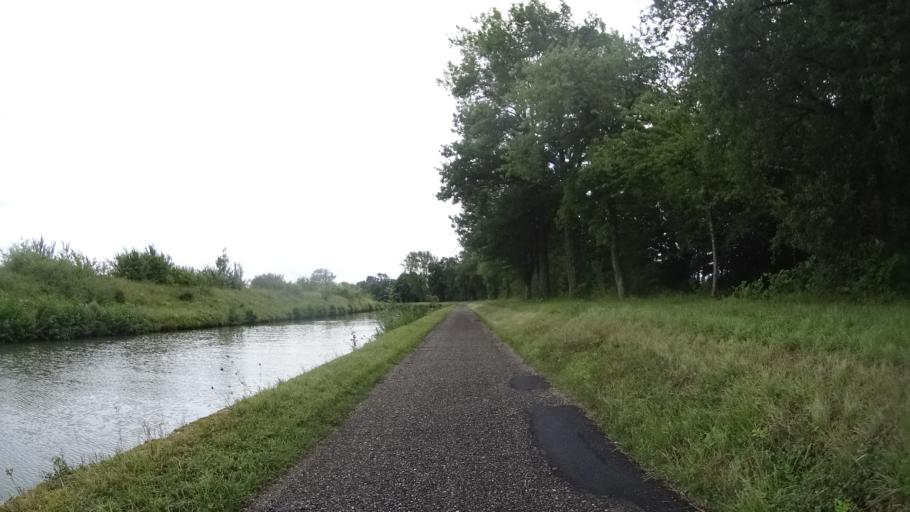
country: FR
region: Lorraine
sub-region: Departement de la Moselle
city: Lorquin
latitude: 48.6971
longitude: 6.9105
